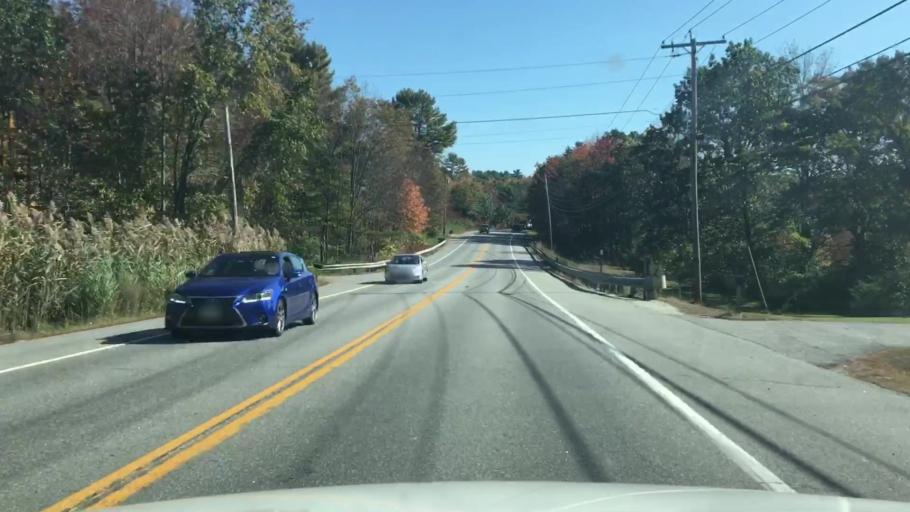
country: US
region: Maine
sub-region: Androscoggin County
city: Lisbon Falls
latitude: 43.9851
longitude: -70.0384
